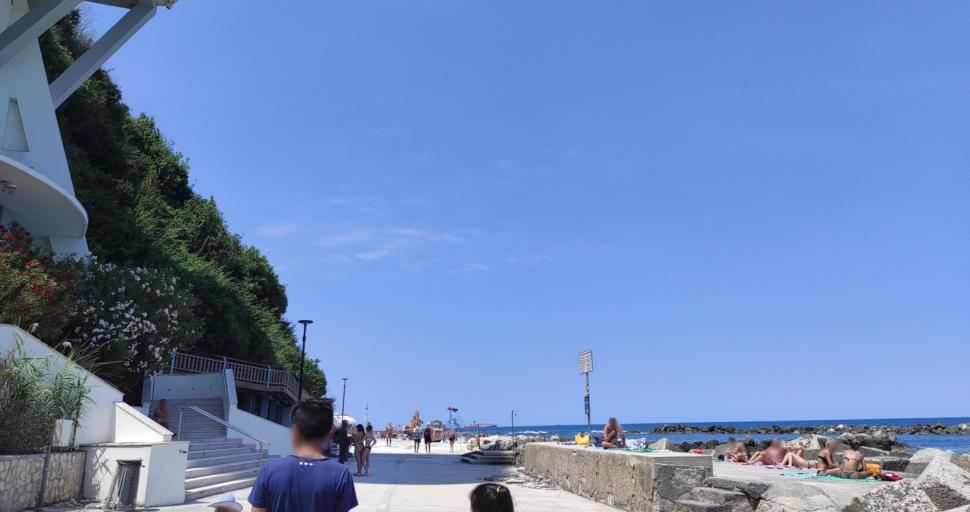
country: IT
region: The Marches
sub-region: Provincia di Ancona
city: Pietra la Croce
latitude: 43.6161
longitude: 13.5341
